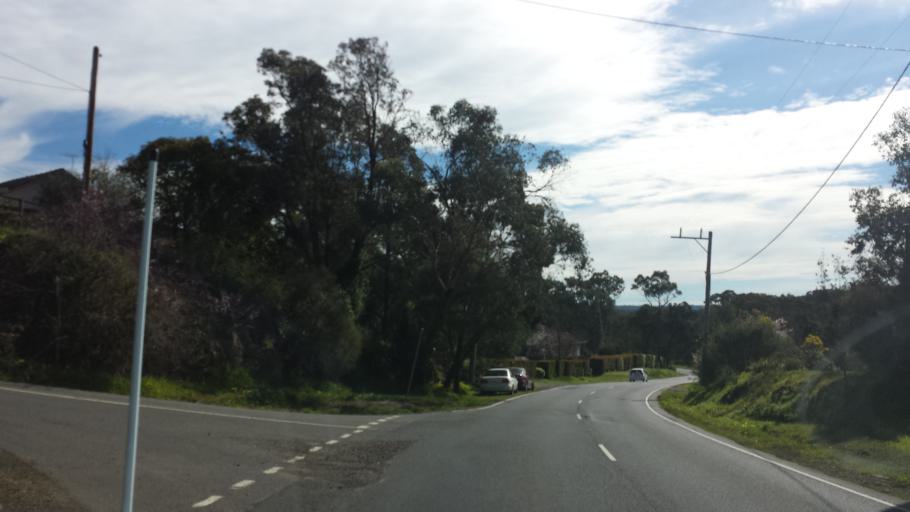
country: AU
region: Victoria
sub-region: Nillumbik
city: Wattleglen
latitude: -37.6743
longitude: 145.1981
